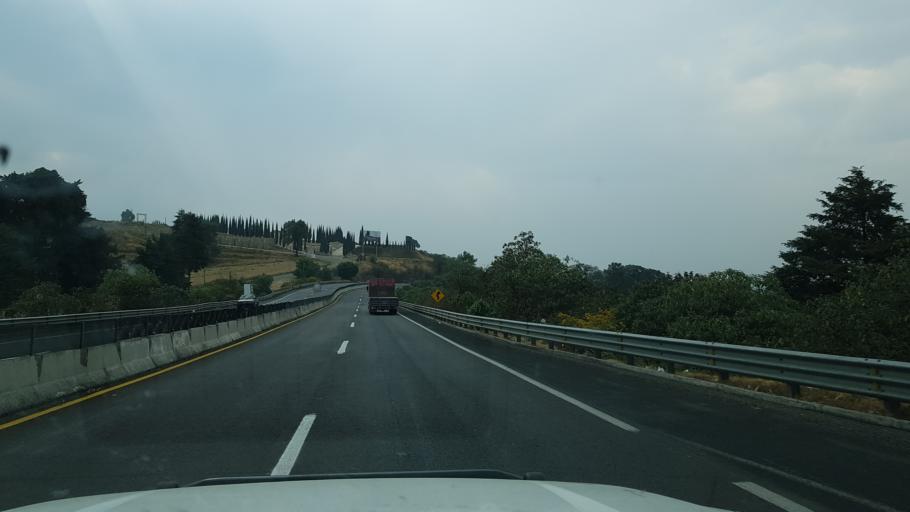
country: MX
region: Mexico
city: Tlalmanalco de Velazquez
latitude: 19.1898
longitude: -98.8016
